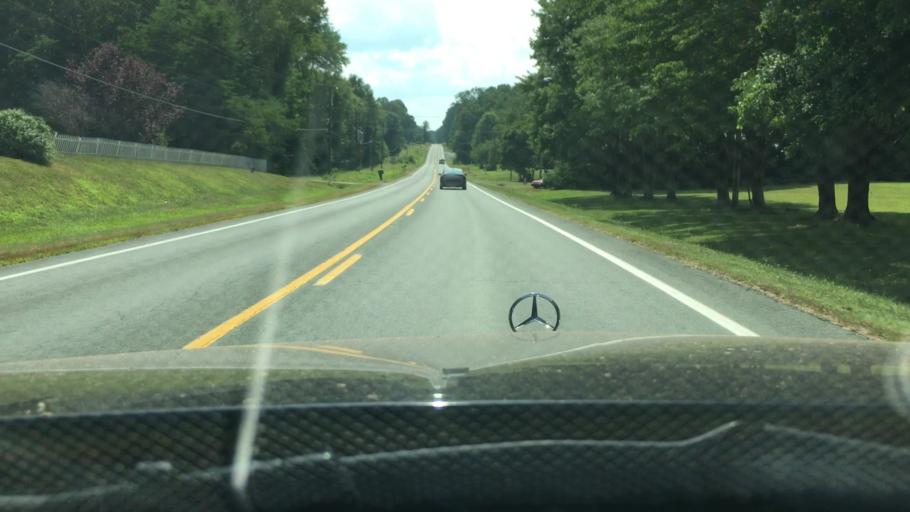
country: US
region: Virginia
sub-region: Orange County
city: Orange
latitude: 38.2583
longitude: -78.0064
